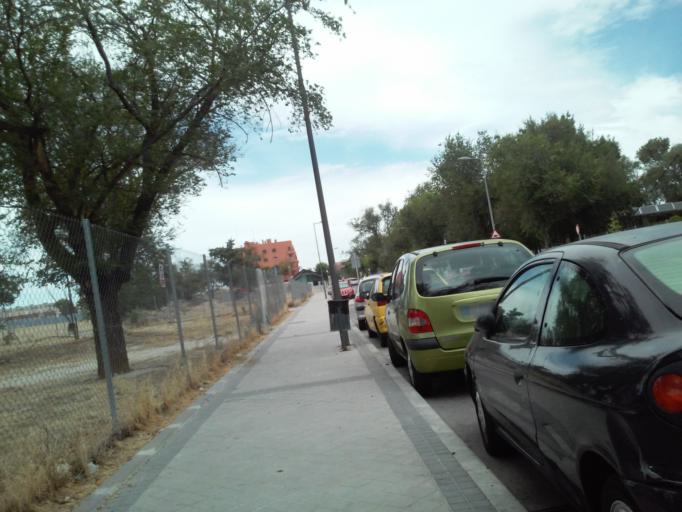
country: ES
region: Madrid
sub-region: Provincia de Madrid
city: Valdemoro
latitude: 40.1948
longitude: -3.6800
